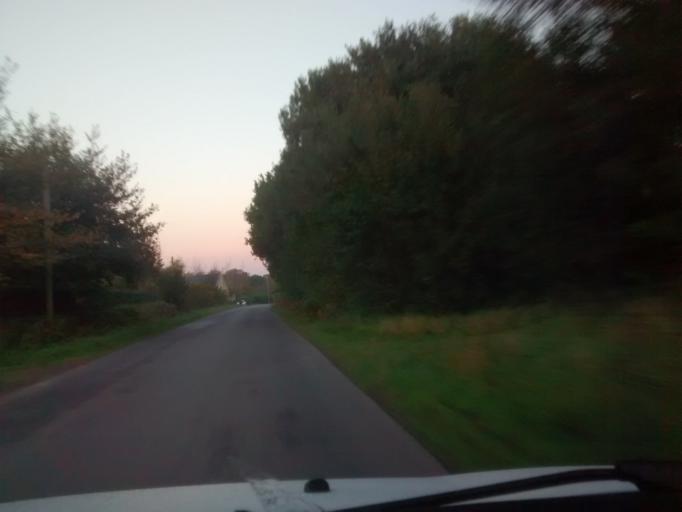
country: FR
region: Brittany
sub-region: Departement des Cotes-d'Armor
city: Trevou-Treguignec
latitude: 48.8006
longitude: -3.3496
